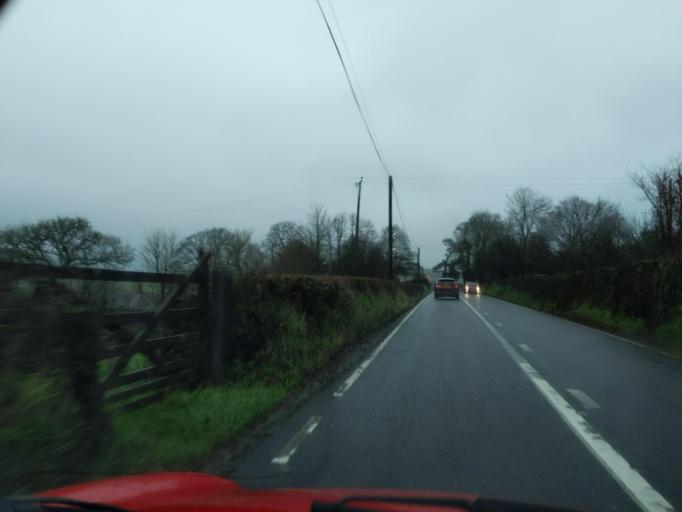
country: GB
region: England
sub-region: Cornwall
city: Launceston
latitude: 50.6078
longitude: -4.3376
